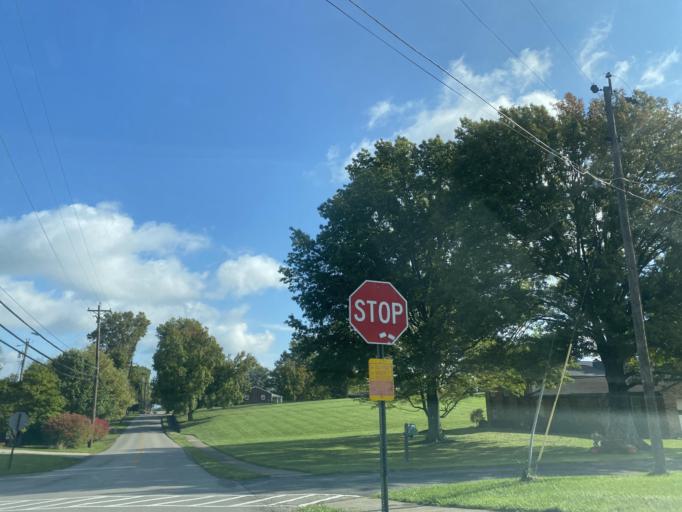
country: US
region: Kentucky
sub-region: Campbell County
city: Cold Spring
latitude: 39.0221
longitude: -84.4244
